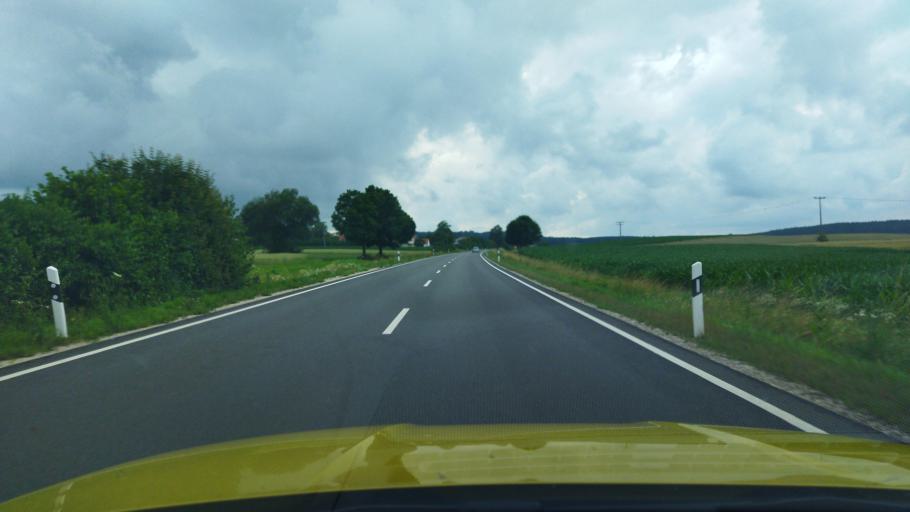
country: DE
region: Bavaria
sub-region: Regierungsbezirk Mittelfranken
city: Absberg
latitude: 49.1098
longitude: 10.8976
